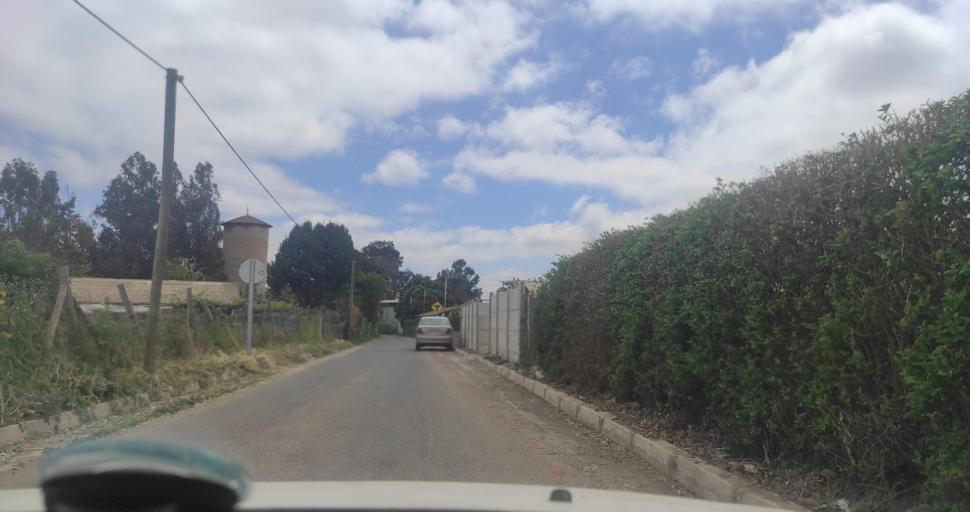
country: CL
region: Valparaiso
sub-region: Provincia de Marga Marga
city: Limache
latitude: -33.0163
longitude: -71.2418
